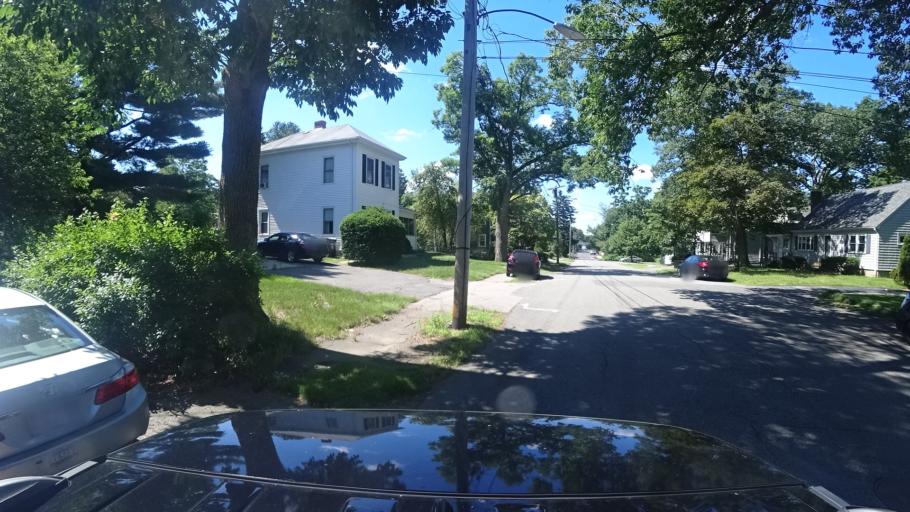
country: US
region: Massachusetts
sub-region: Norfolk County
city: Dedham
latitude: 42.2560
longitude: -71.1497
